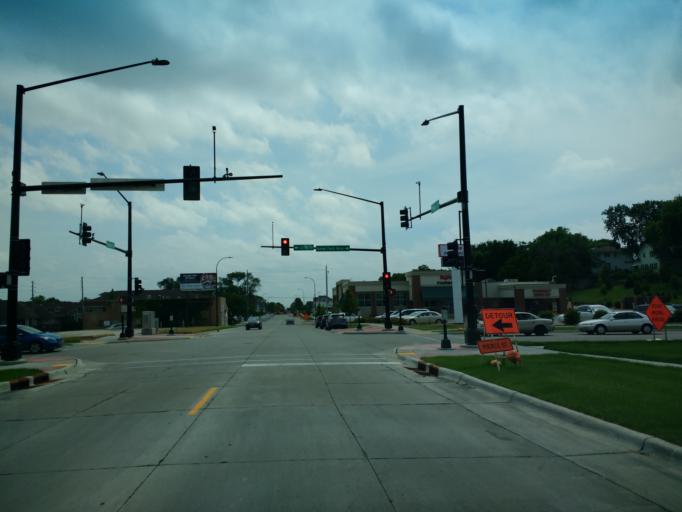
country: US
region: Iowa
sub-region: Woodbury County
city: Sioux City
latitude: 42.5184
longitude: -96.4052
